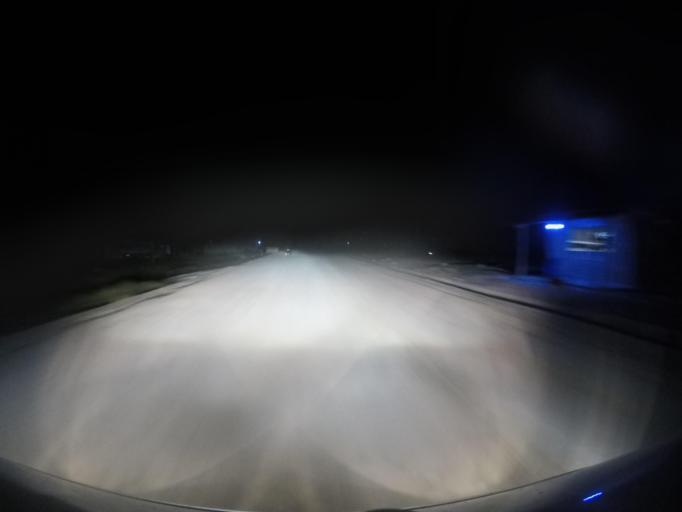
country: TL
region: Viqueque
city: Viqueque
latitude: -8.8041
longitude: 126.5472
